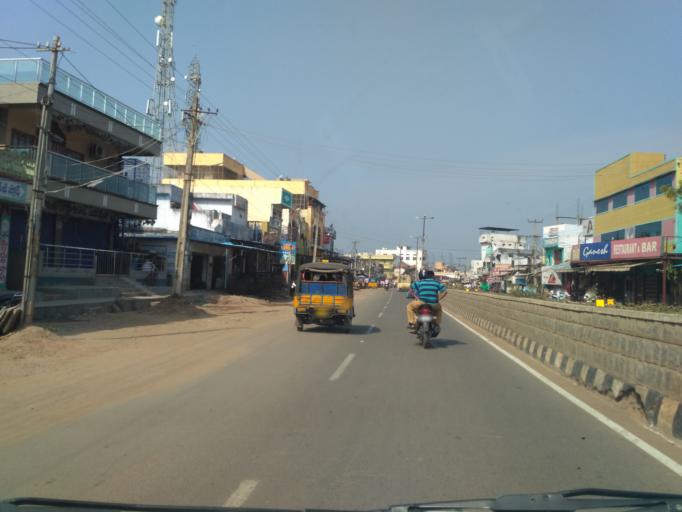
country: IN
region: Telangana
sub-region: Khammam
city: Yellandu
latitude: 17.5856
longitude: 80.3261
